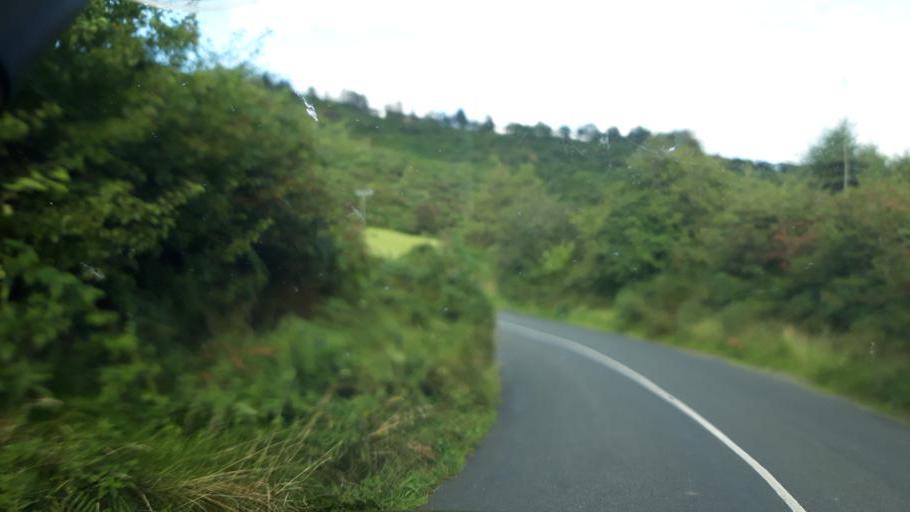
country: GB
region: Northern Ireland
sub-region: Down District
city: Warrenpoint
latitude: 54.0367
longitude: -6.2749
